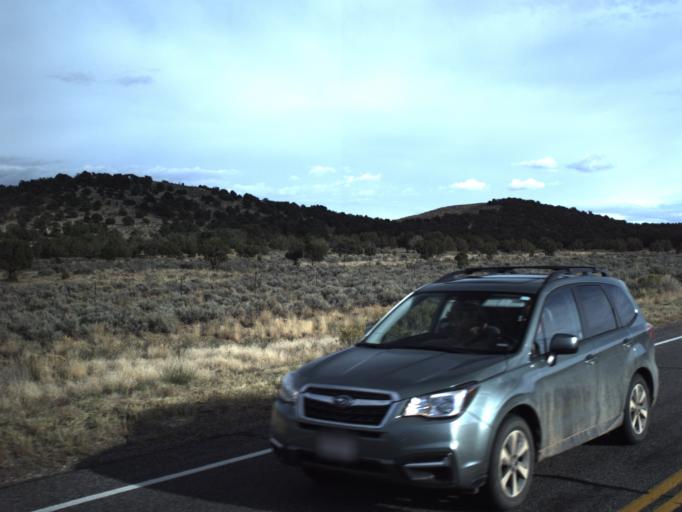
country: US
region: Utah
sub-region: Sevier County
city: Aurora
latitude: 39.0131
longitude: -112.0312
